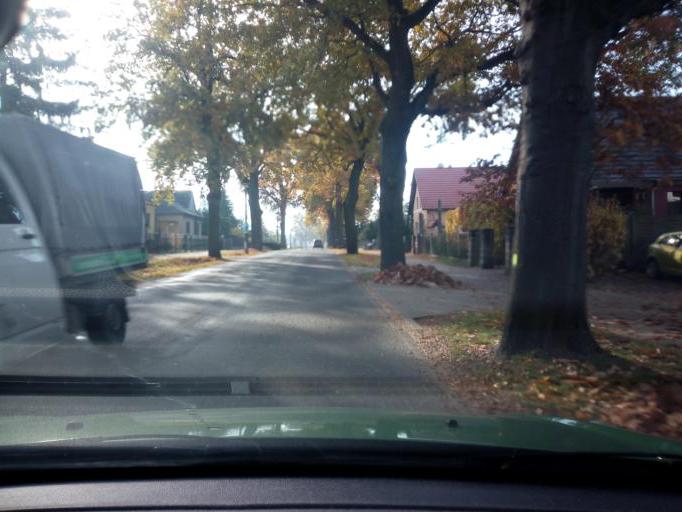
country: DE
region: Brandenburg
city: Neuenhagen
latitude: 52.5088
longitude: 13.7067
